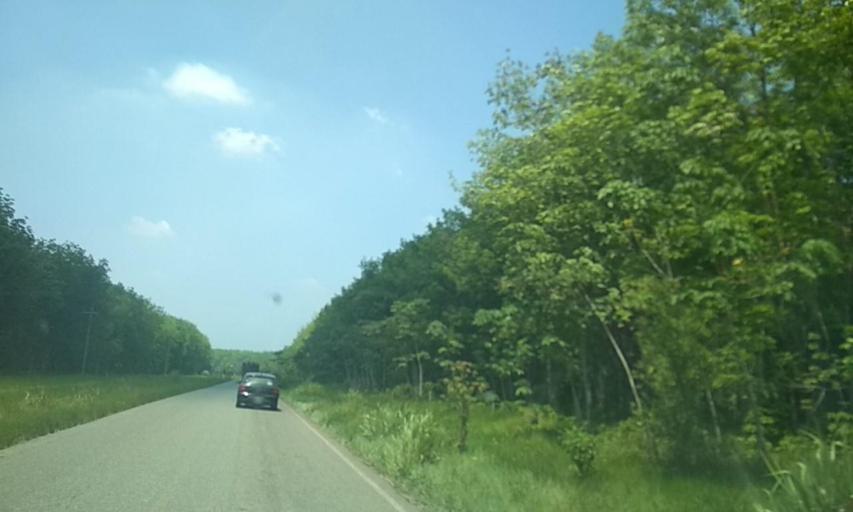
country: MX
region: Tabasco
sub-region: Huimanguillo
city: Paso de la Mina 2da. Seccion (Barrial)
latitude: 17.8097
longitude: -93.6177
